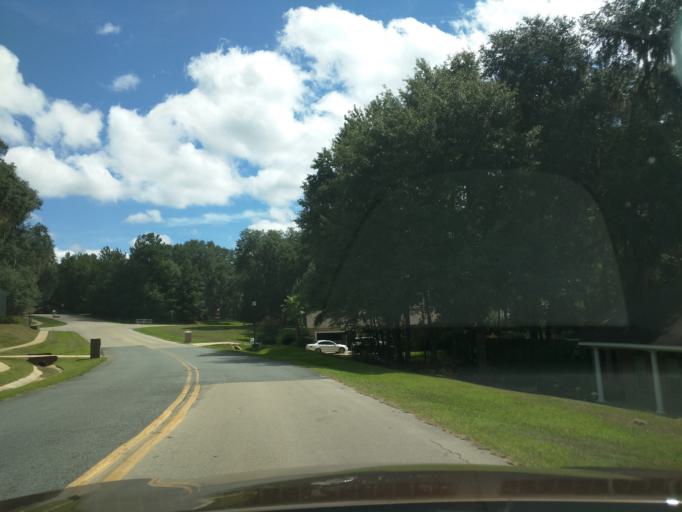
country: US
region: Florida
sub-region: Leon County
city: Tallahassee
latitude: 30.5701
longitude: -84.2534
